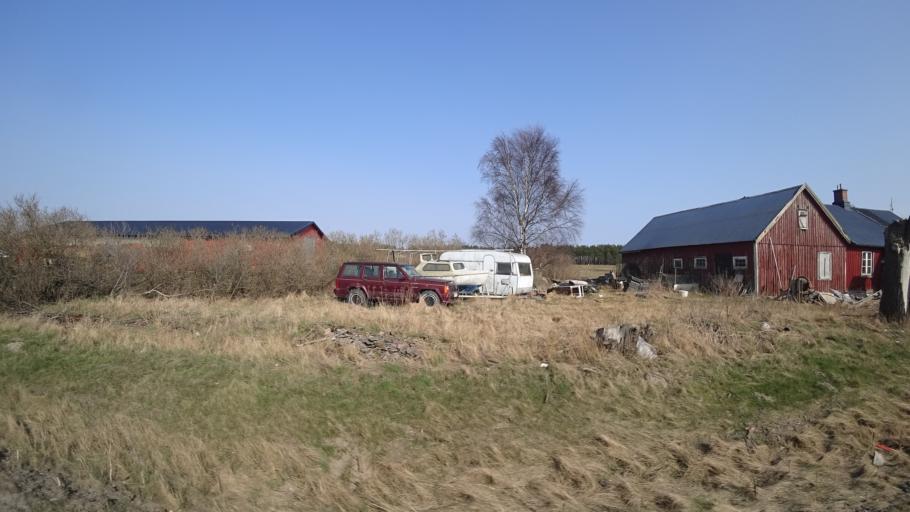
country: SE
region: Skane
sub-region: Kristianstads Kommun
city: Ahus
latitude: 55.9707
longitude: 14.2744
